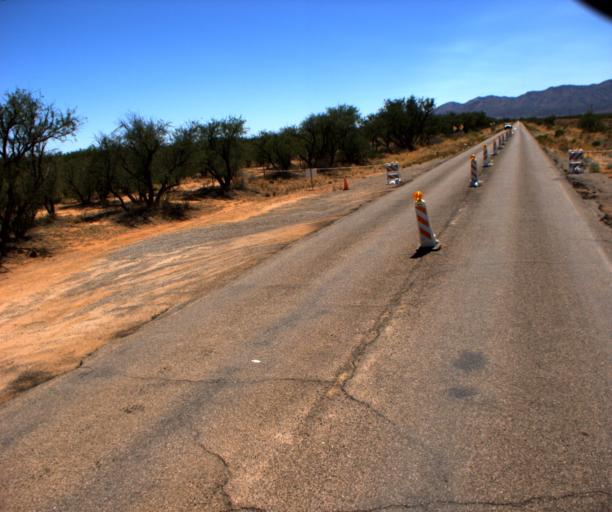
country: US
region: Arizona
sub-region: Pima County
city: Three Points
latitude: 31.8283
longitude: -111.4250
